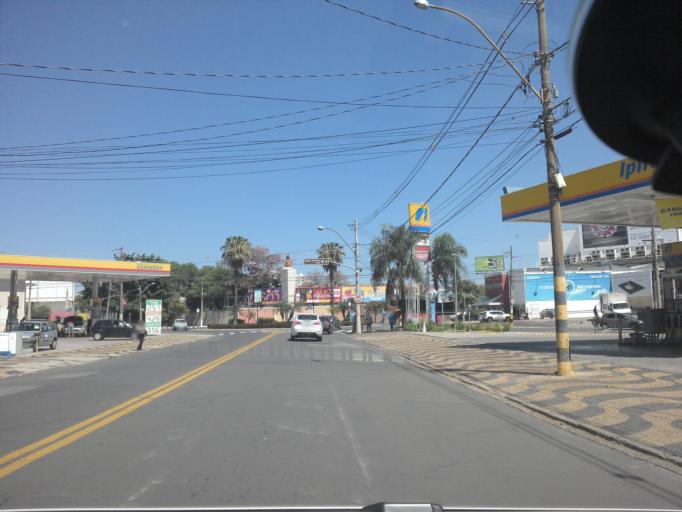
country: BR
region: Sao Paulo
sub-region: Campinas
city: Campinas
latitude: -22.8820
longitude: -47.0553
